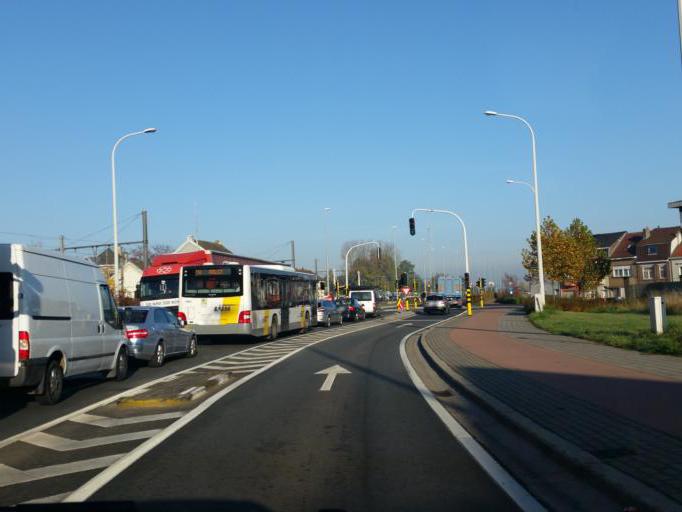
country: BE
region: Flanders
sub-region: Provincie Vlaams-Brabant
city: Asse
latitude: 50.9053
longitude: 4.2094
